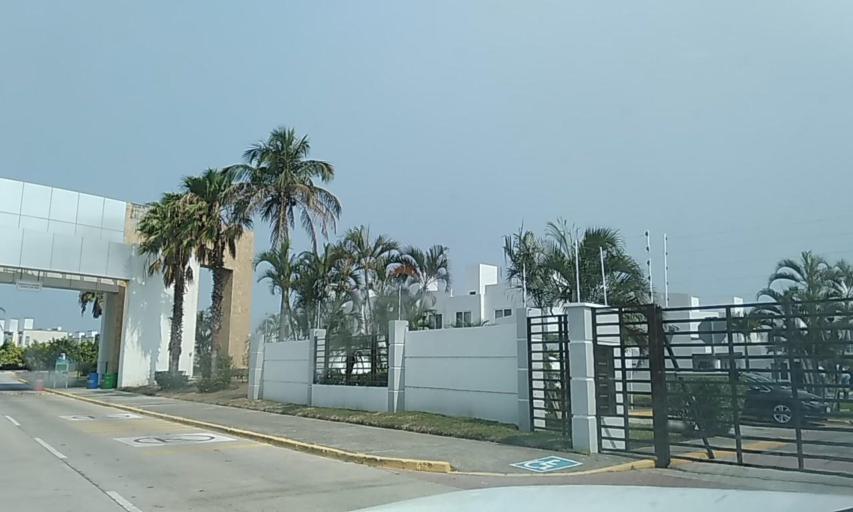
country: MX
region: Veracruz
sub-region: Veracruz
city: Hacienda Sotavento
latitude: 19.1331
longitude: -96.1731
